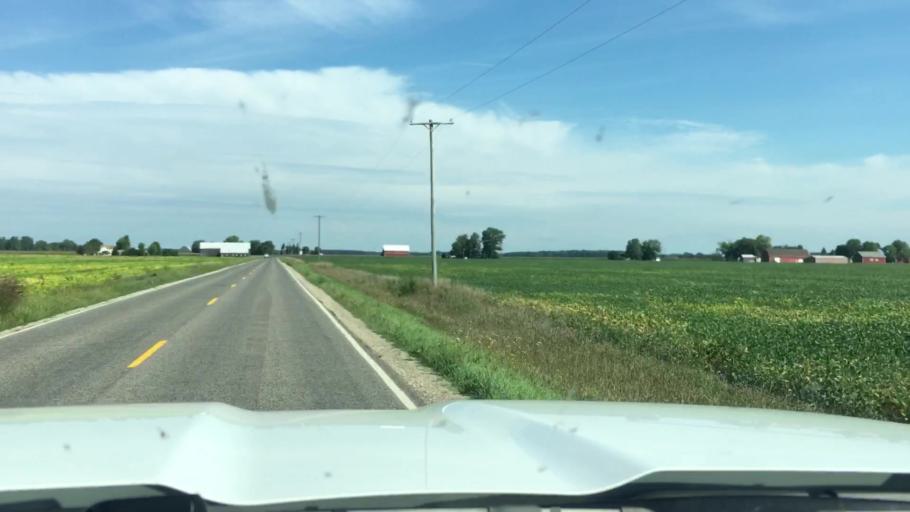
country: US
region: Michigan
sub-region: Saginaw County
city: Hemlock
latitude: 43.5043
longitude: -84.2296
